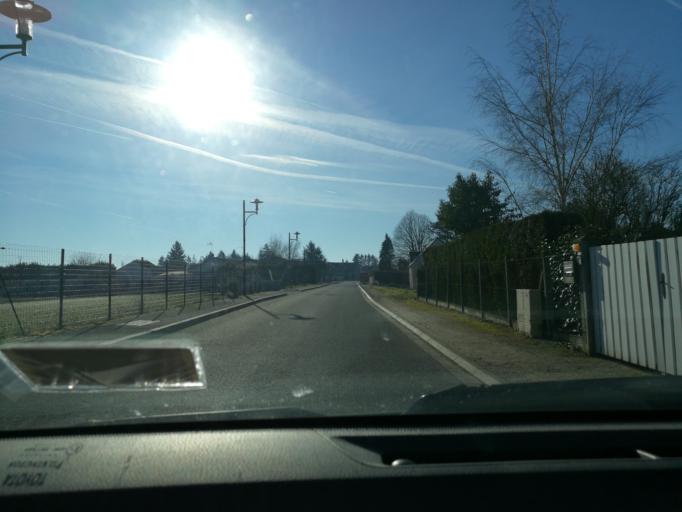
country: FR
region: Centre
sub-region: Departement du Loiret
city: Chaingy
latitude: 47.8806
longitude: 1.7646
